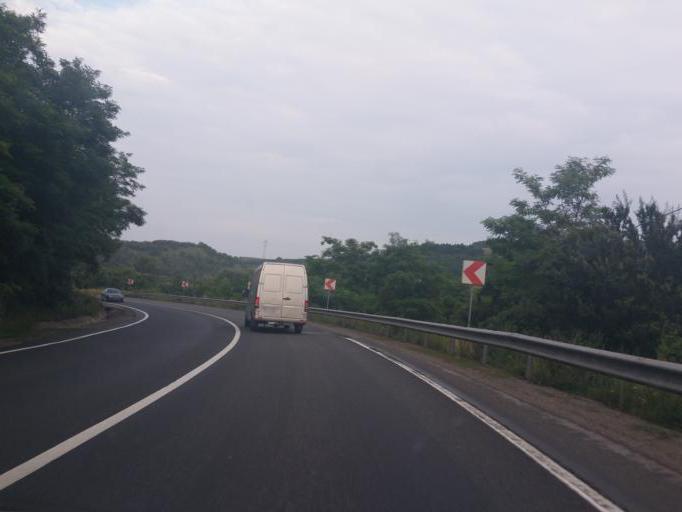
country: RO
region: Cluj
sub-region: Comuna Baciu
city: Suceagu
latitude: 46.7958
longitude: 23.4894
